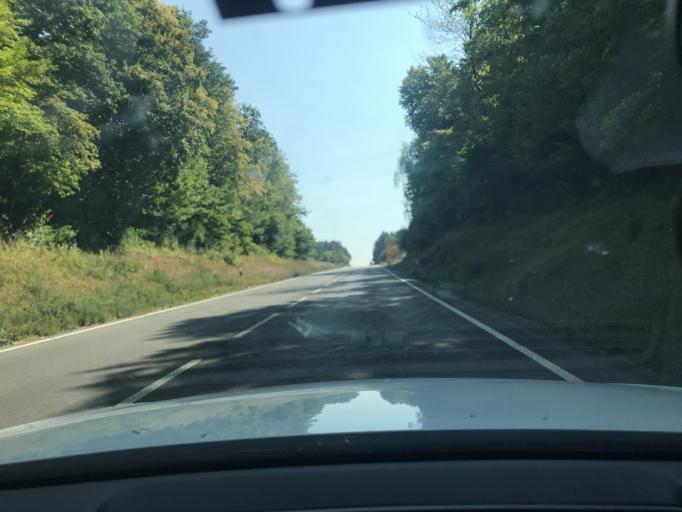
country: DE
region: Bavaria
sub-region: Upper Palatinate
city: Sulzbach-Rosenberg
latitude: 49.4744
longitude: 11.7469
